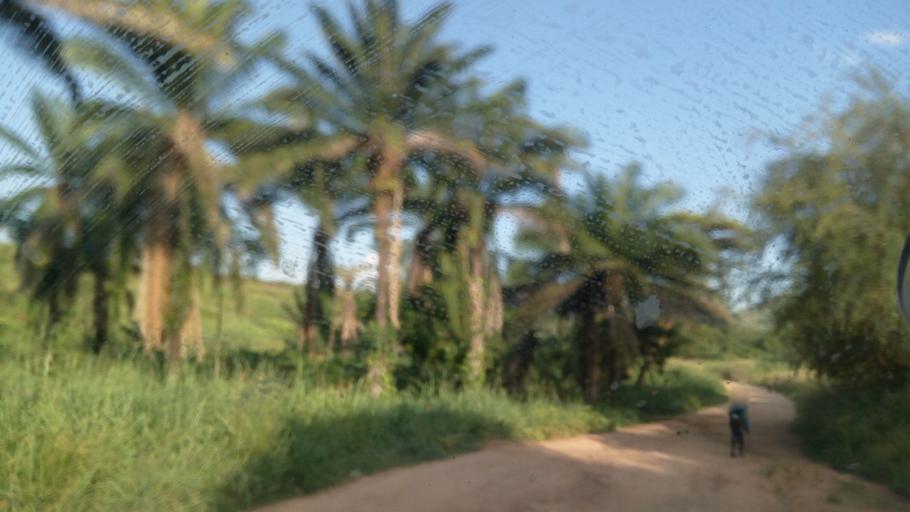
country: BI
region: Bururi
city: Rumonge
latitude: -4.2045
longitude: 29.0076
